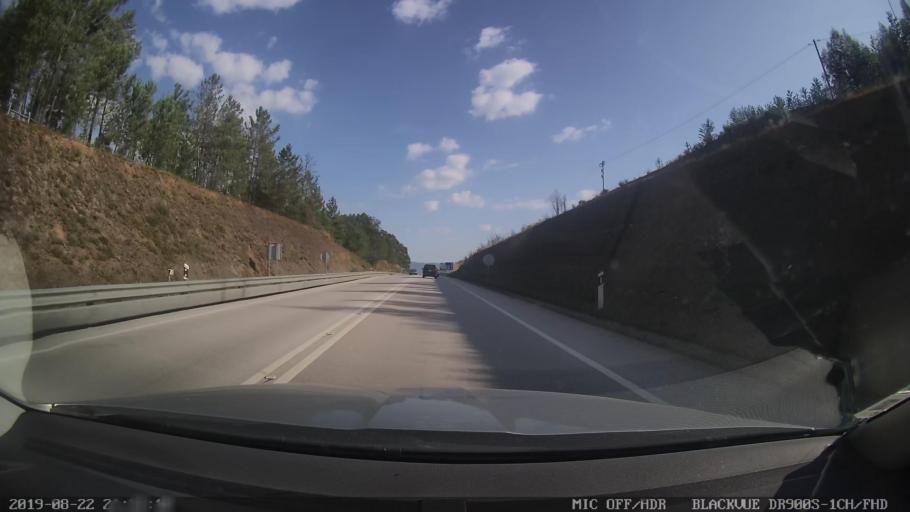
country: PT
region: Leiria
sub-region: Pedrogao Grande
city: Pedrogao Grande
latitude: 39.8887
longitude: -8.1208
